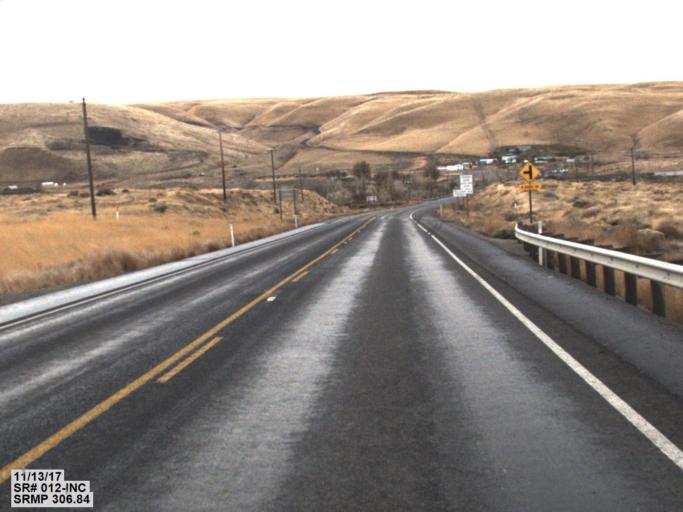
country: US
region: Washington
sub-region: Benton County
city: Finley
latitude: 46.0674
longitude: -118.9080
